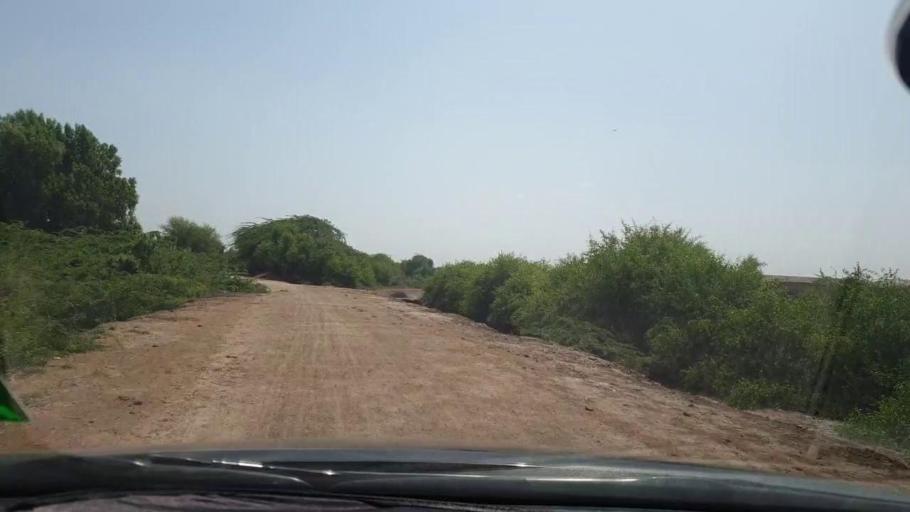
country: PK
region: Sindh
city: Tando Bago
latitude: 24.9216
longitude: 69.0839
